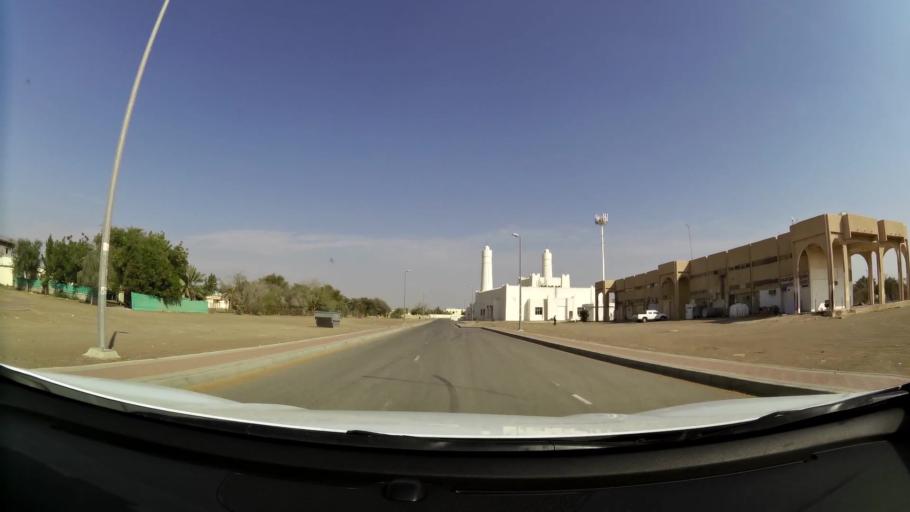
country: AE
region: Abu Dhabi
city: Al Ain
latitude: 24.0921
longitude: 55.9238
